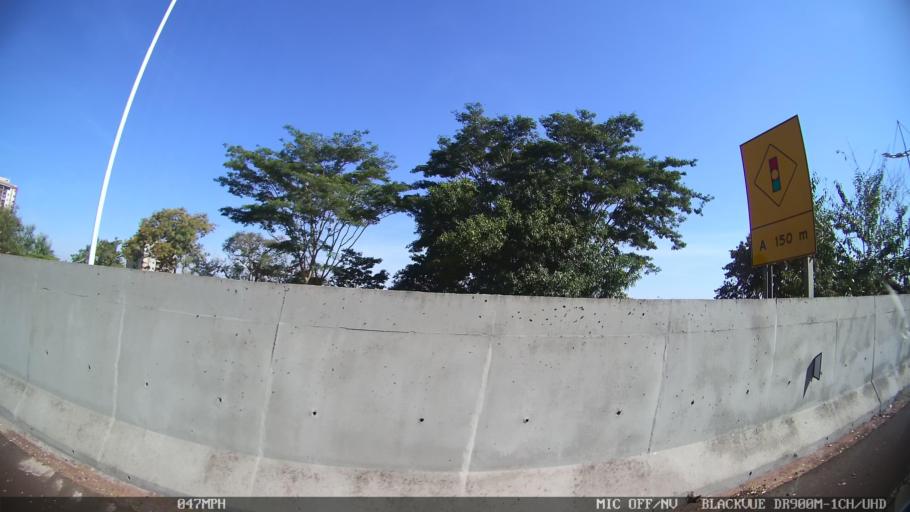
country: BR
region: Sao Paulo
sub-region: Ribeirao Preto
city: Ribeirao Preto
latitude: -21.1884
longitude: -47.7833
